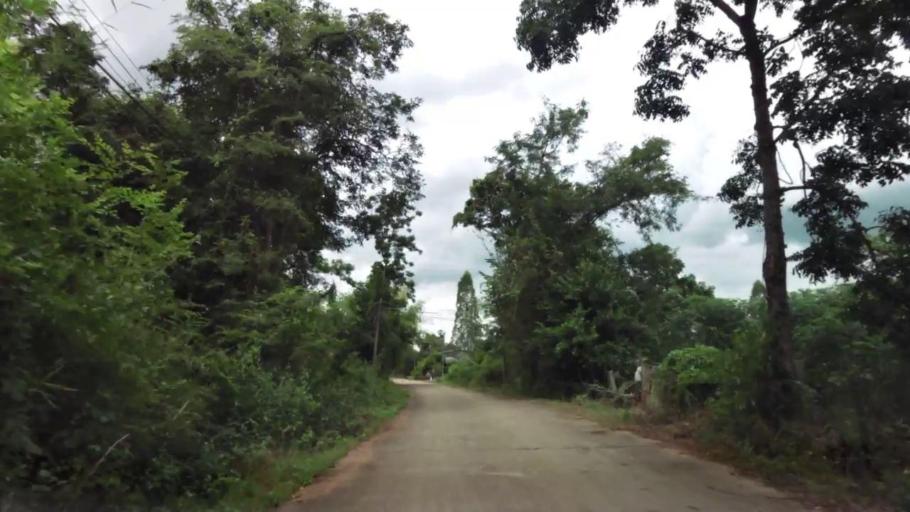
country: TH
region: Nakhon Sawan
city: Phai Sali
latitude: 15.6040
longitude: 100.6596
